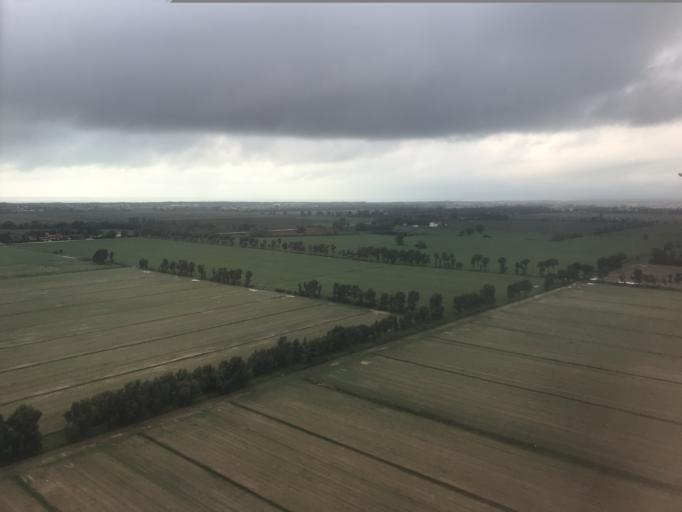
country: IT
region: Latium
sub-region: Citta metropolitana di Roma Capitale
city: Maccarese
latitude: 41.8573
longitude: 12.2571
